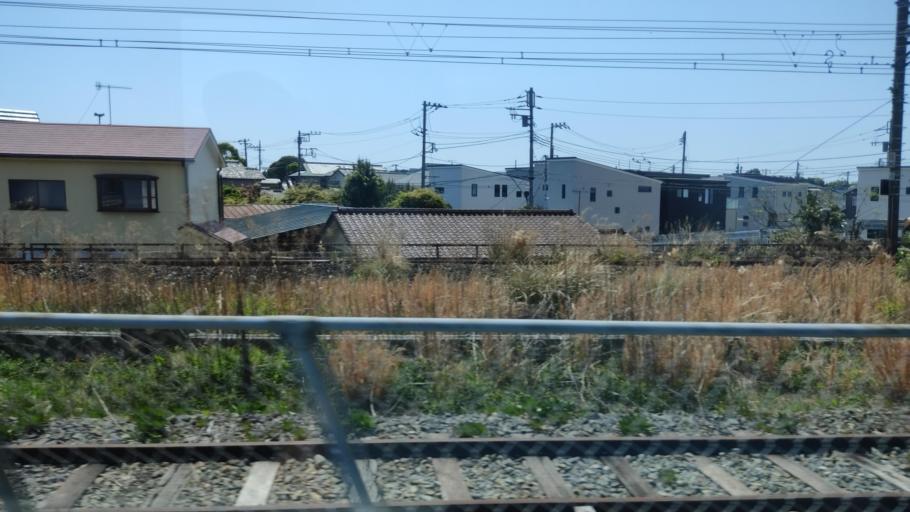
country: JP
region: Kanagawa
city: Chigasaki
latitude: 35.3318
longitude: 139.3748
